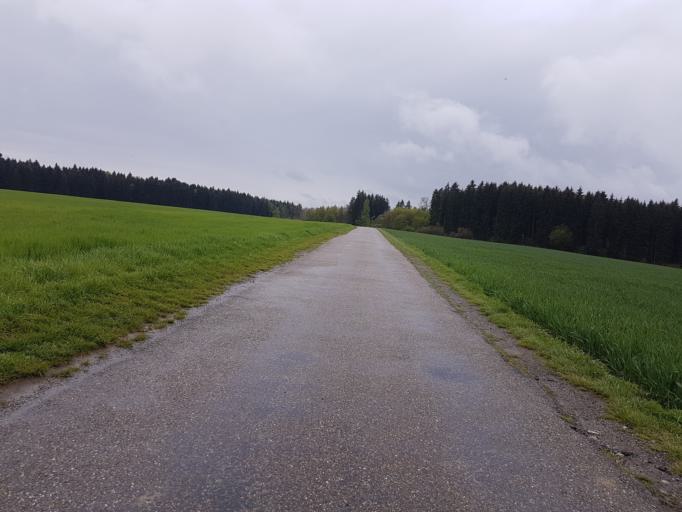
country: DE
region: Baden-Wuerttemberg
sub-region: Freiburg Region
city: Rottweil
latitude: 48.1887
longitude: 8.6169
